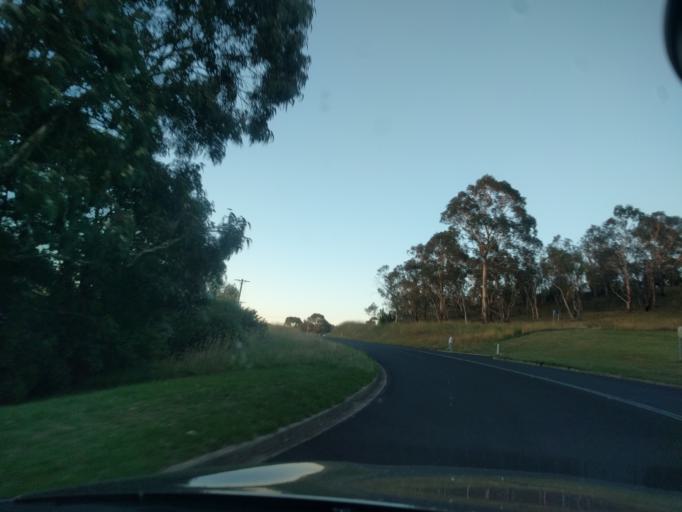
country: AU
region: New South Wales
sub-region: Armidale Dumaresq
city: Armidale
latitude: -30.5045
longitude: 151.6617
